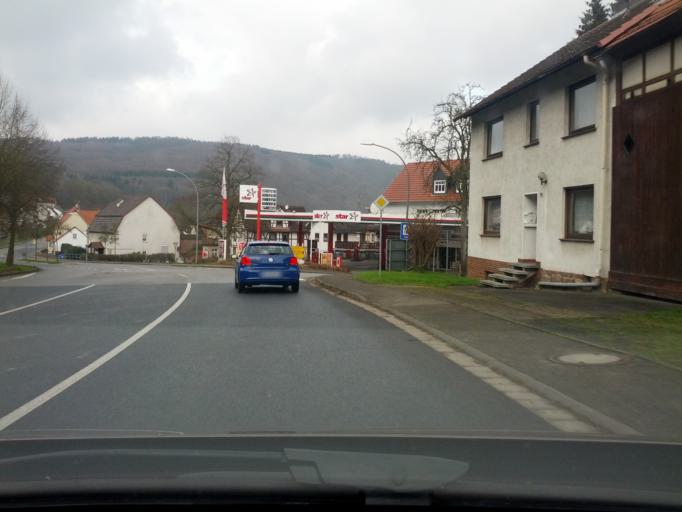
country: DE
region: Lower Saxony
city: Bodenfelde
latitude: 51.5967
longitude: 9.5491
